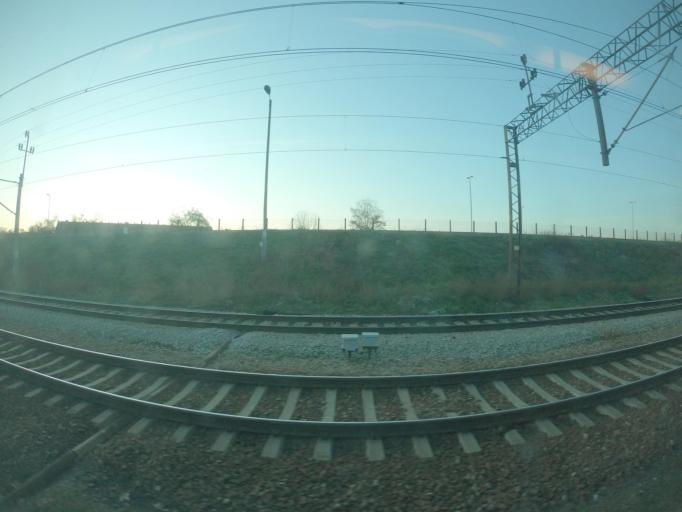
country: PL
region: Lubusz
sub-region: Powiat gorzowski
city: Kostrzyn nad Odra
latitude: 52.5943
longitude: 14.6484
